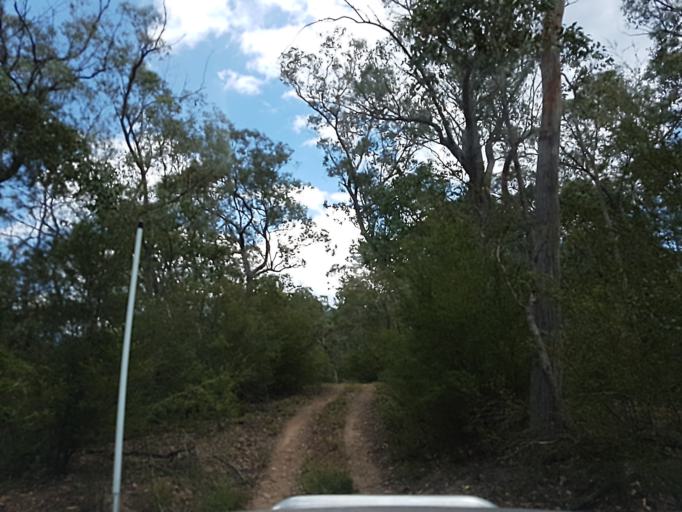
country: AU
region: Victoria
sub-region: East Gippsland
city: Lakes Entrance
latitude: -37.3633
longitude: 148.3554
